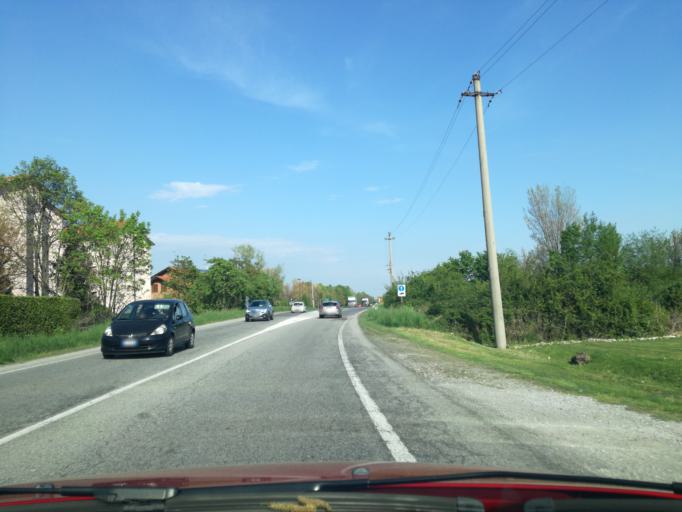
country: IT
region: Lombardy
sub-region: Provincia di Monza e Brianza
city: Bellusco
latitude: 45.6156
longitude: 9.4292
